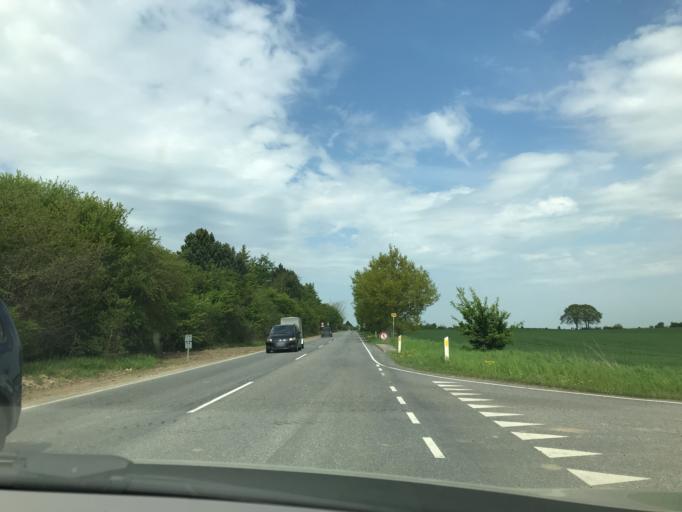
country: DK
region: South Denmark
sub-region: Assens Kommune
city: Assens
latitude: 55.2773
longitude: 9.9206
